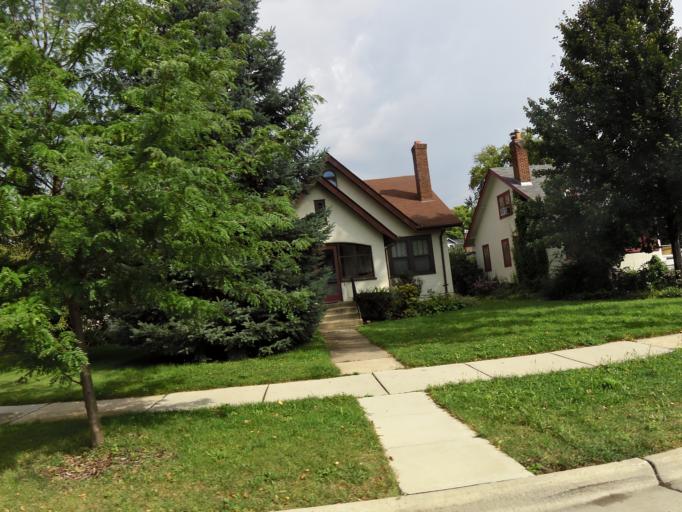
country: US
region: Minnesota
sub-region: Dakota County
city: Mendota Heights
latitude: 44.9307
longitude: -93.1762
